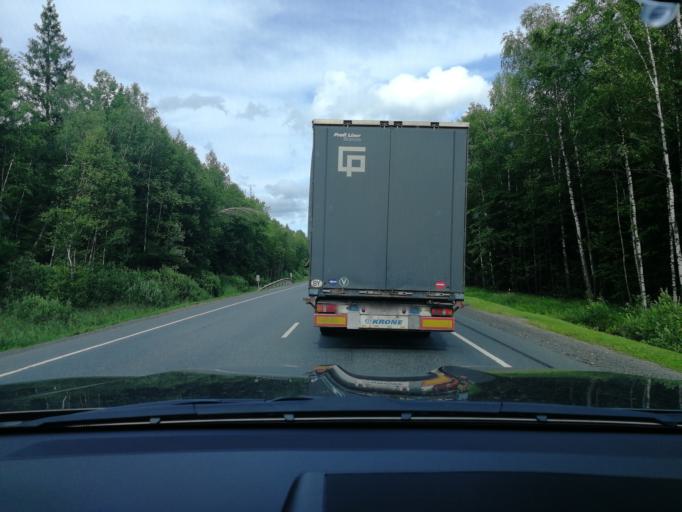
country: RU
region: Moskovskaya
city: Popovo
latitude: 55.0422
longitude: 37.6873
